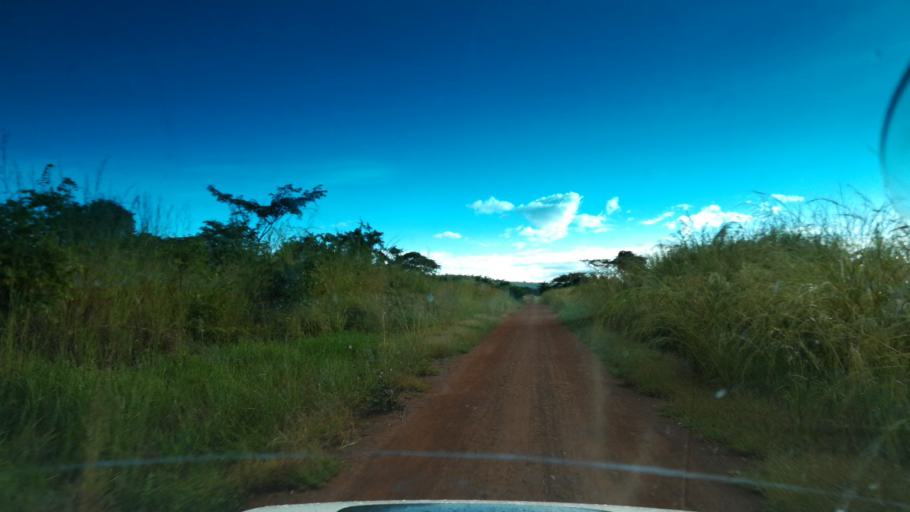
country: ZM
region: Northern
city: Kaputa
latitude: -8.4000
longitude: 28.9409
